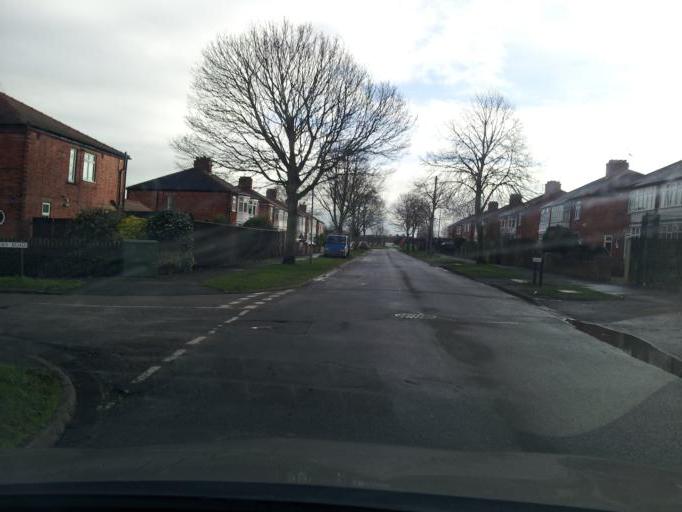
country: GB
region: England
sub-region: Nottinghamshire
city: Newark on Trent
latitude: 53.0669
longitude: -0.8119
